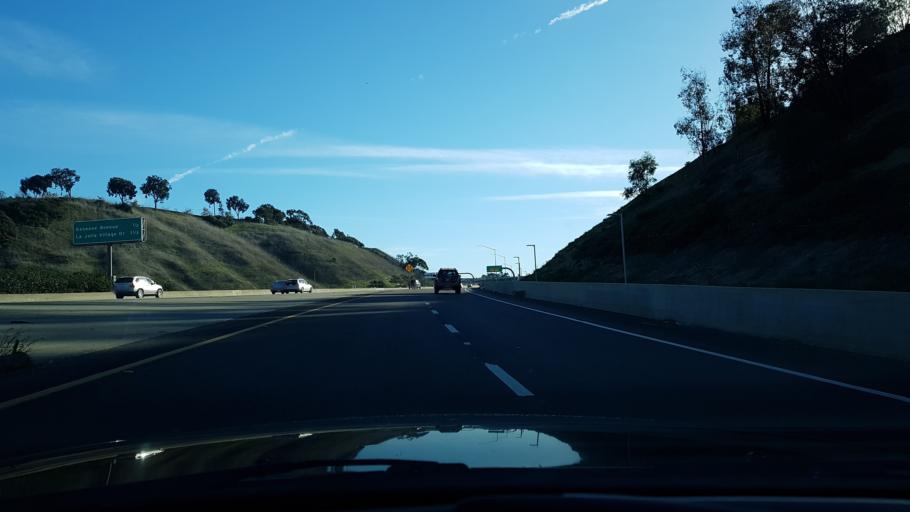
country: US
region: California
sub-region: San Diego County
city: La Jolla
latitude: 32.8985
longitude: -117.2256
